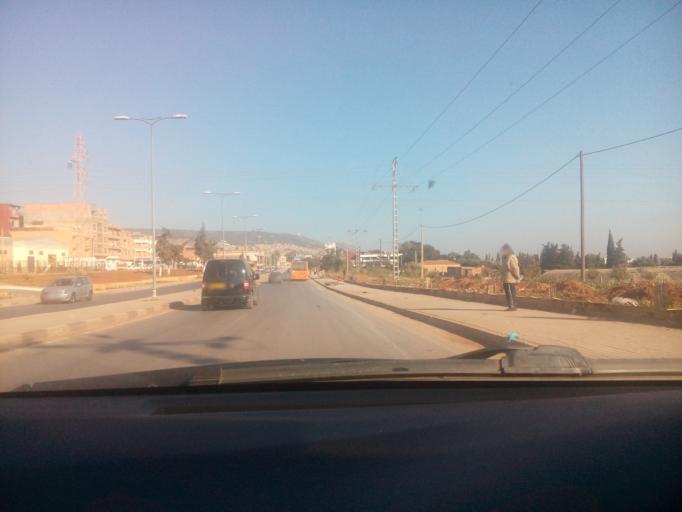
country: DZ
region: Oran
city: Oran
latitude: 35.6656
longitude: -0.6834
